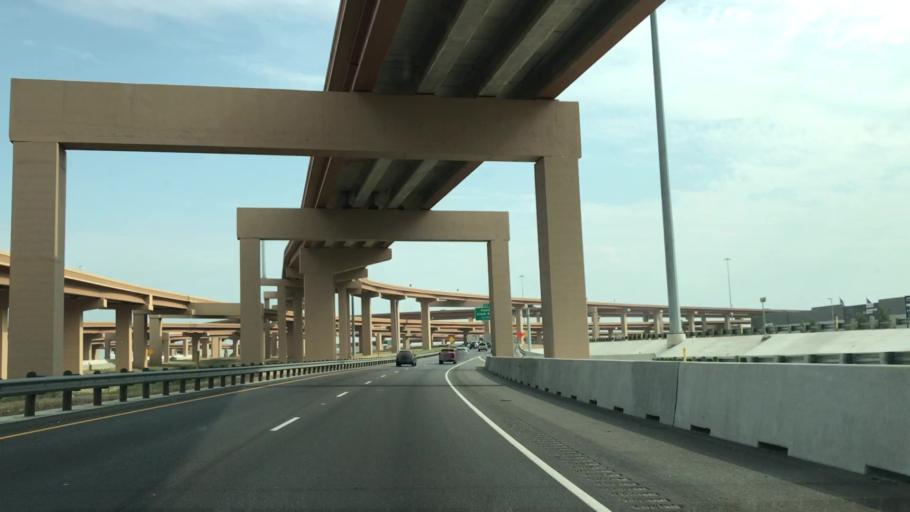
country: US
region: Texas
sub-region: Tarrant County
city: Blue Mound
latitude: 32.8348
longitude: -97.3123
